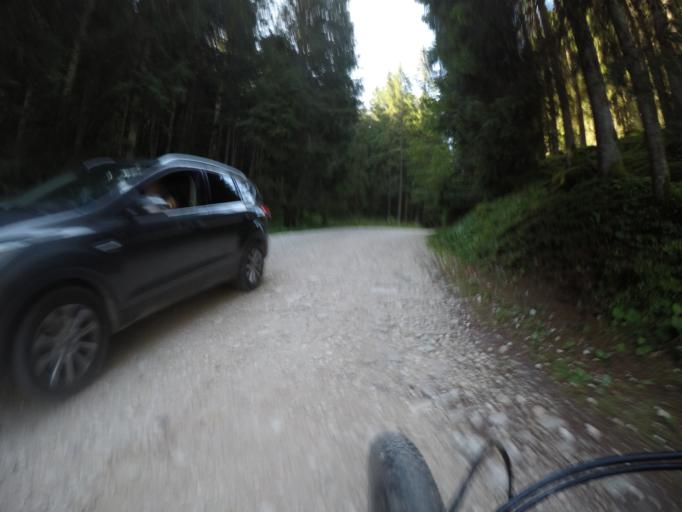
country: IT
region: Veneto
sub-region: Provincia di Vicenza
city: Asiago
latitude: 45.8433
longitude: 11.5241
